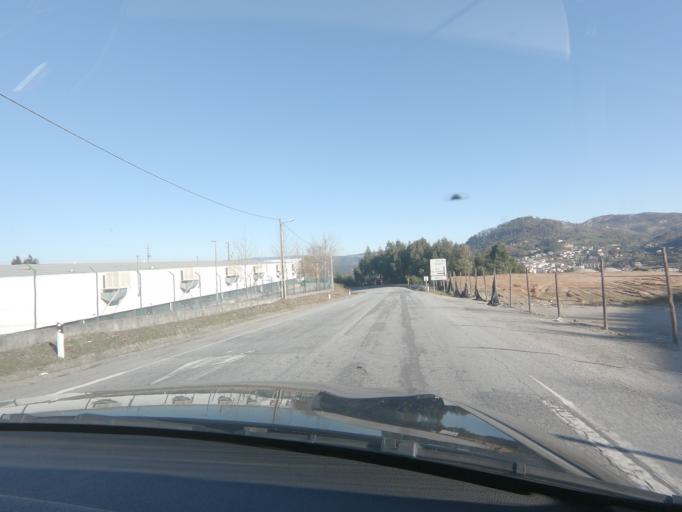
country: PT
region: Viseu
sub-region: Vouzela
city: Vouzela
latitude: 40.7257
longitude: -8.1269
